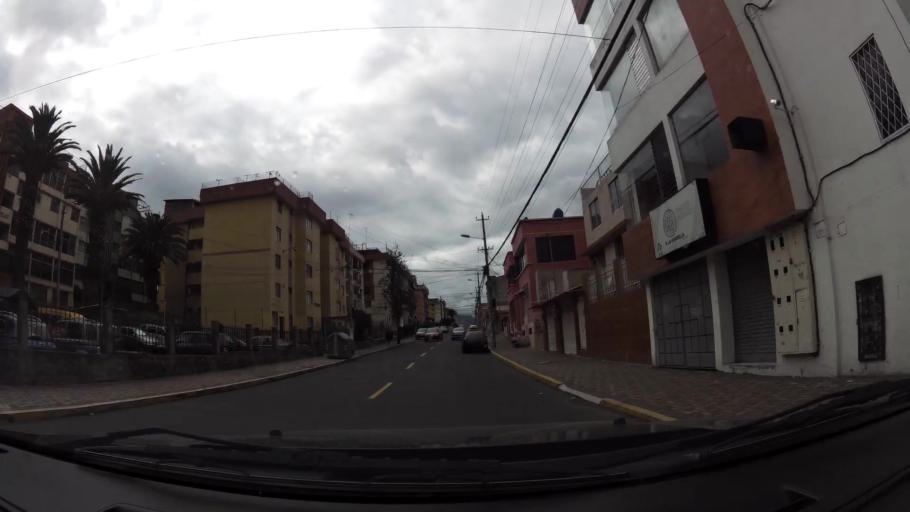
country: EC
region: Pichincha
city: Quito
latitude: -0.1269
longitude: -78.5019
